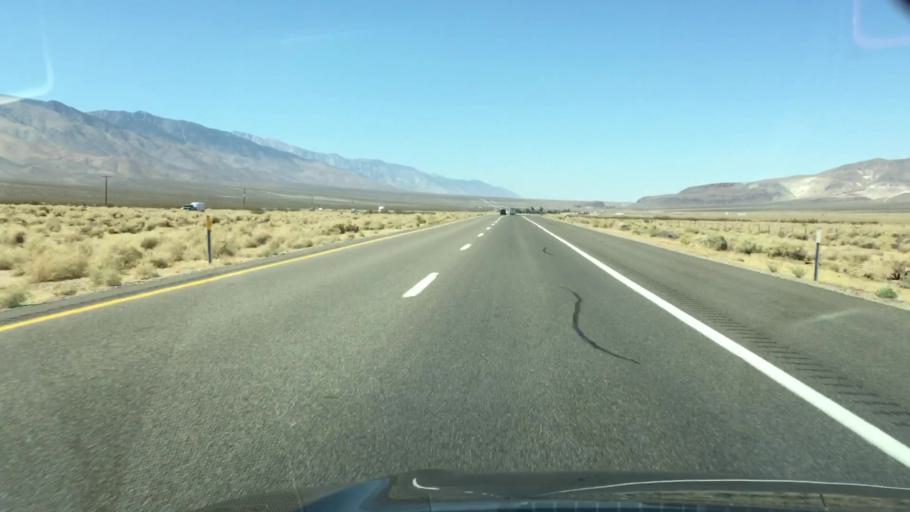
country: US
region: California
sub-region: Kern County
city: Inyokern
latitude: 36.0280
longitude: -117.9414
